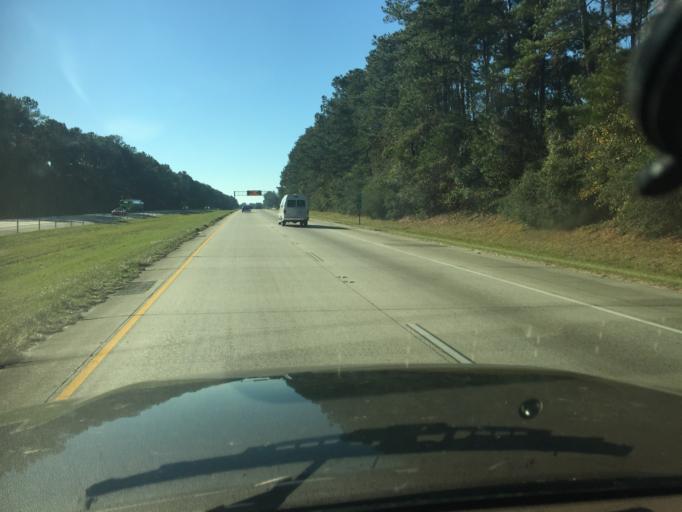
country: US
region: Louisiana
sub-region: Saint Tammany Parish
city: Pearl River
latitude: 30.3354
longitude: -89.7379
